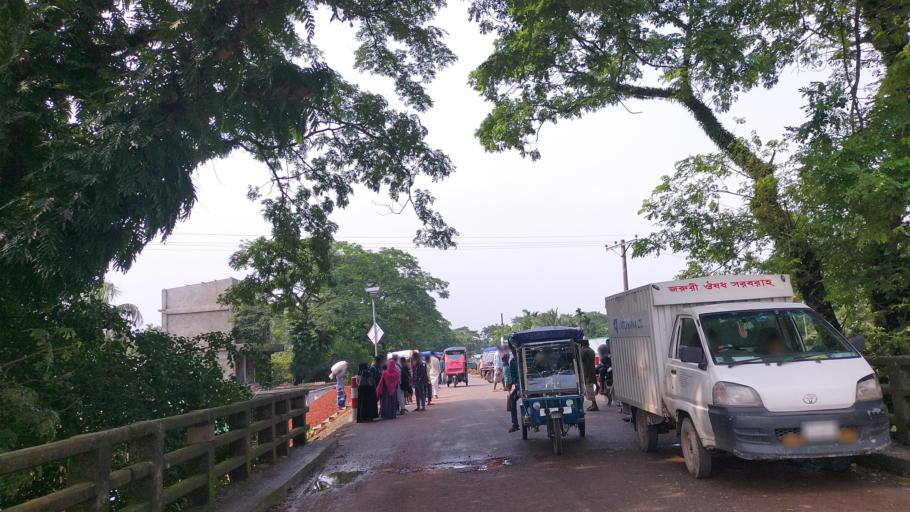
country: BD
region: Dhaka
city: Netrakona
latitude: 24.9548
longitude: 90.8344
